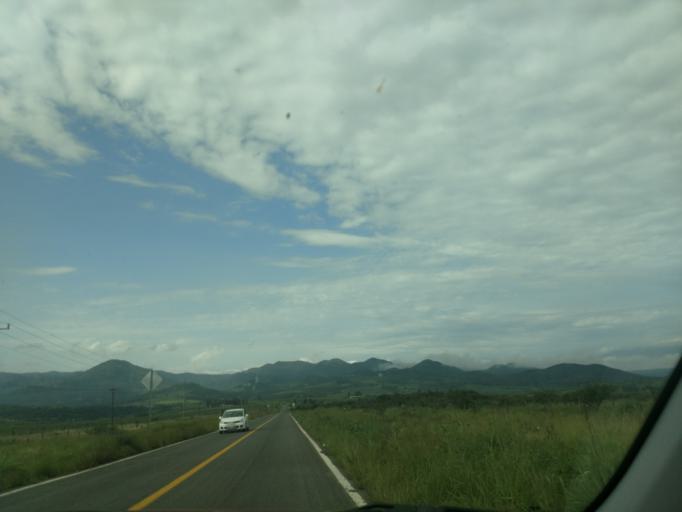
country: MX
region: Jalisco
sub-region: Atengo
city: Soyatlan del Oro
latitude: 20.5354
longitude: -104.3144
